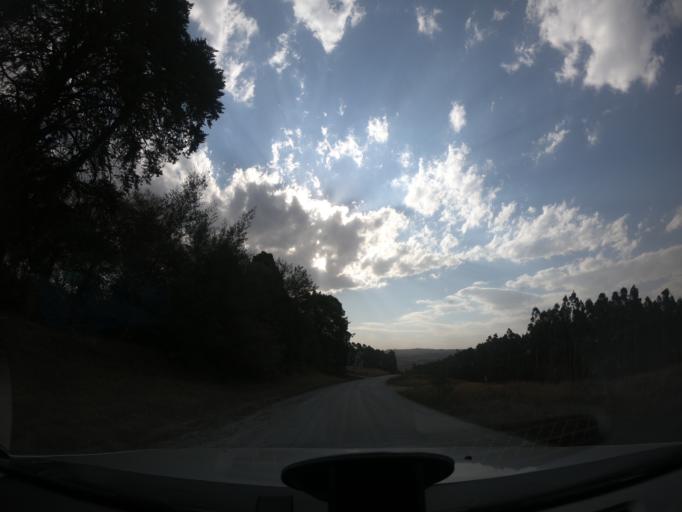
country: ZA
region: KwaZulu-Natal
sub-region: uMgungundlovu District Municipality
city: Howick
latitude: -29.4249
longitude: 30.1054
